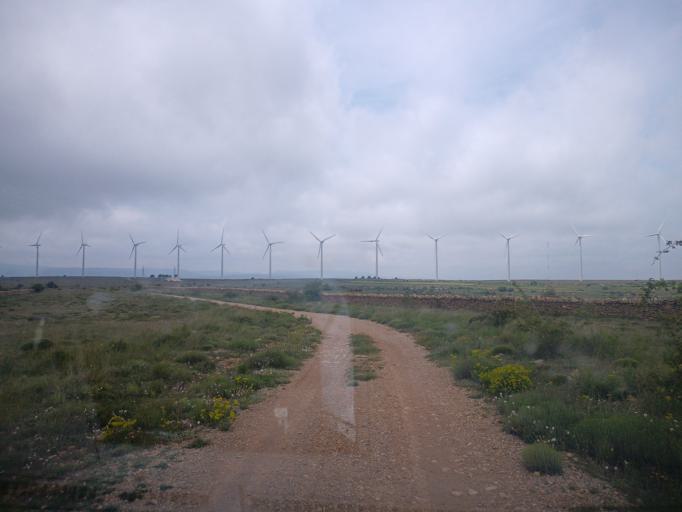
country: ES
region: Valencia
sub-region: Provincia de Castello
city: Castellfort
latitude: 40.4664
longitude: -0.1978
